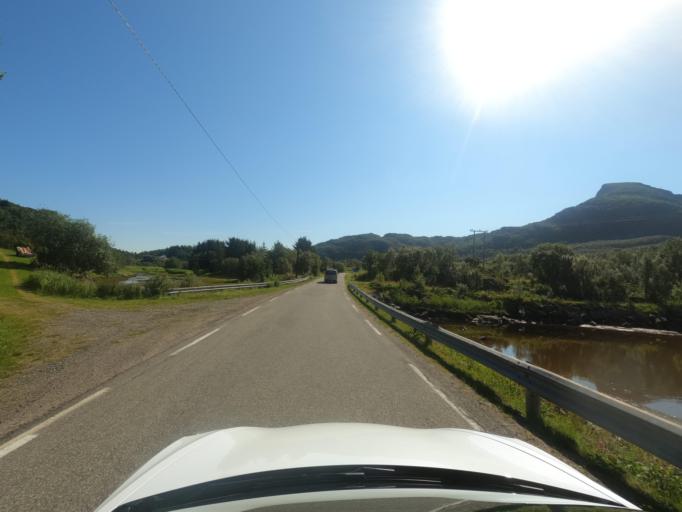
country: NO
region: Nordland
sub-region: Hadsel
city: Stokmarknes
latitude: 68.3037
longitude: 15.0127
